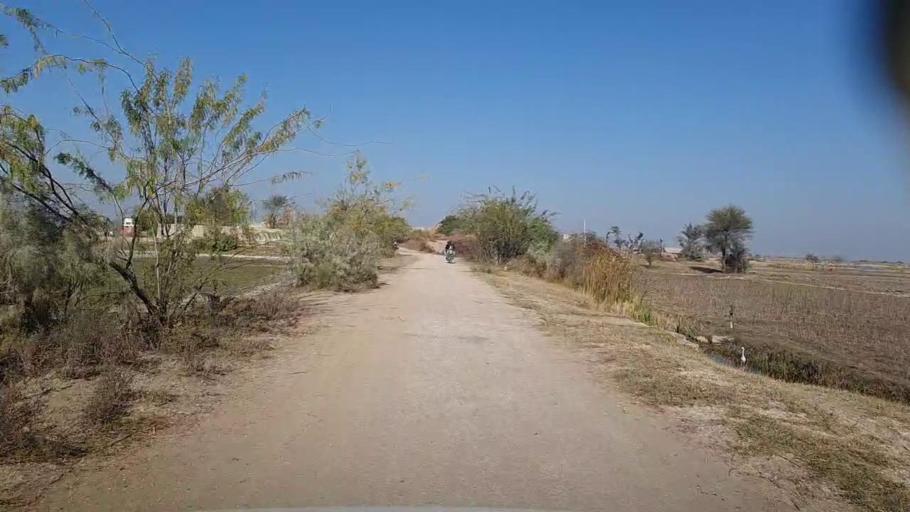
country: PK
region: Sindh
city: Khairpur
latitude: 27.9552
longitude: 69.7504
